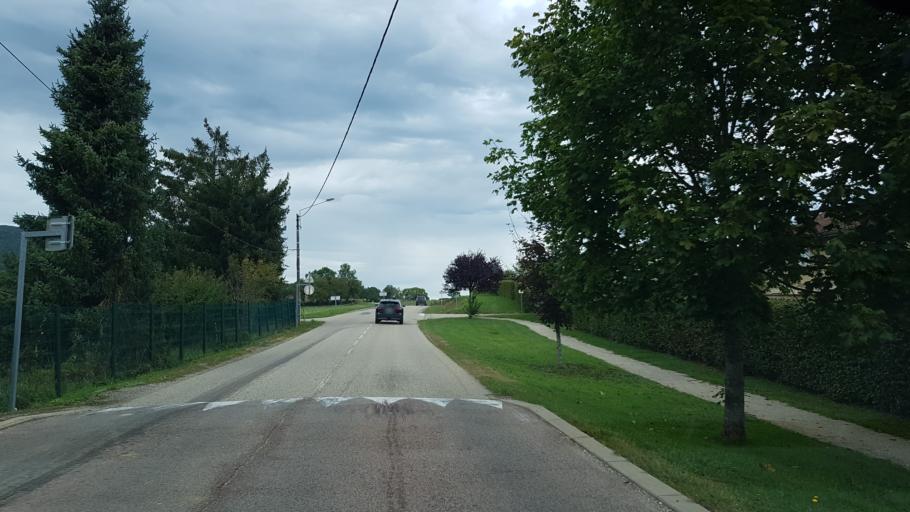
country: FR
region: Rhone-Alpes
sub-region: Departement de l'Ain
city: Cuisiat
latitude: 46.2681
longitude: 5.4267
